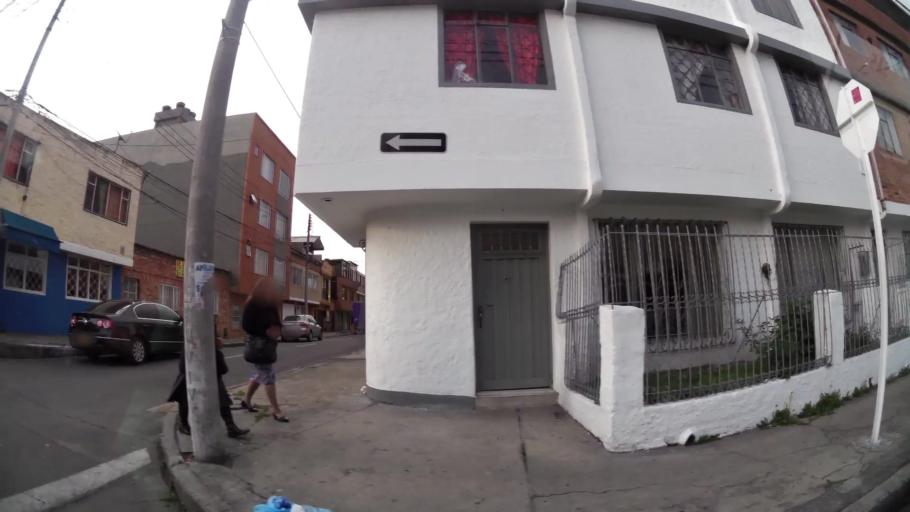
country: CO
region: Bogota D.C.
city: Barrio San Luis
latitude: 4.7228
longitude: -74.0693
